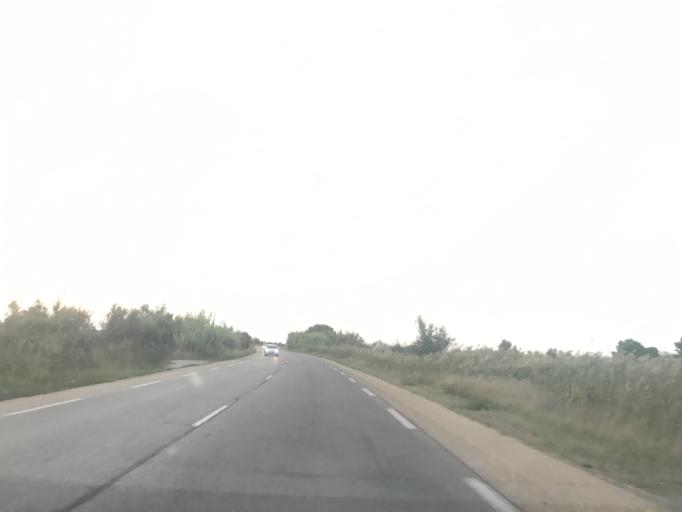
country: FR
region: Provence-Alpes-Cote d'Azur
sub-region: Departement des Bouches-du-Rhone
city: Saintes-Maries-de-la-Mer
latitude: 43.5006
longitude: 4.4027
